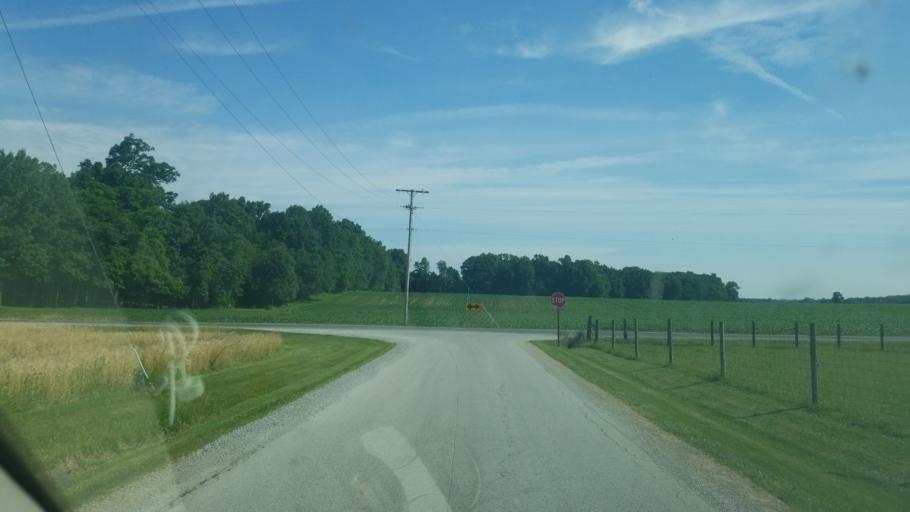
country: US
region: Ohio
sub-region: Wyandot County
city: Upper Sandusky
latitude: 40.8652
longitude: -83.2371
